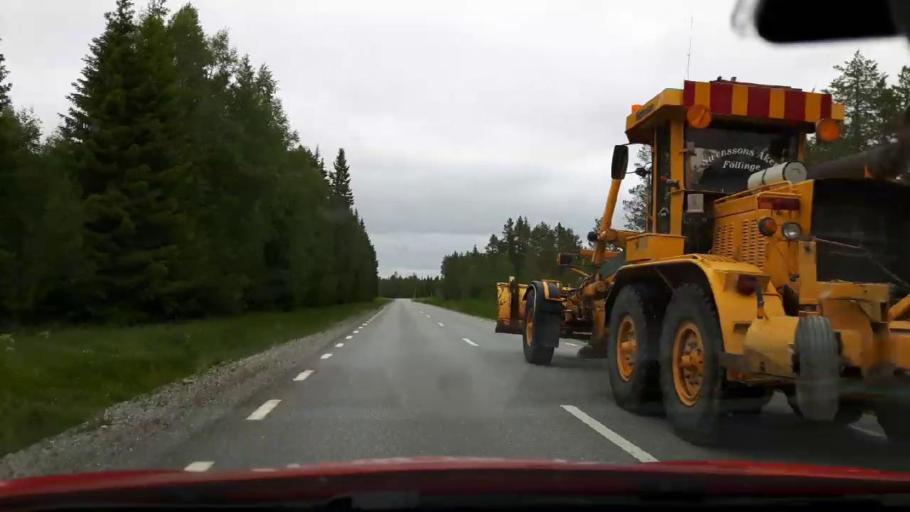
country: SE
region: Jaemtland
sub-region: OEstersunds Kommun
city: Lit
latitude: 63.6898
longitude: 14.6759
